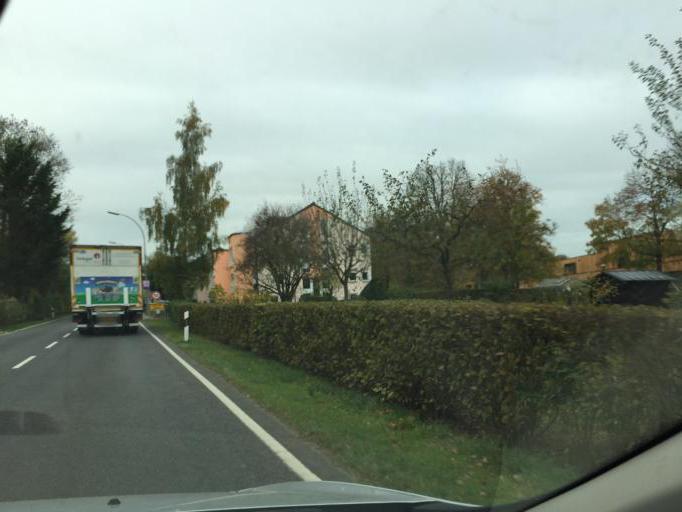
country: LU
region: Luxembourg
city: Capellen
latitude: 49.6477
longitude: 5.9873
